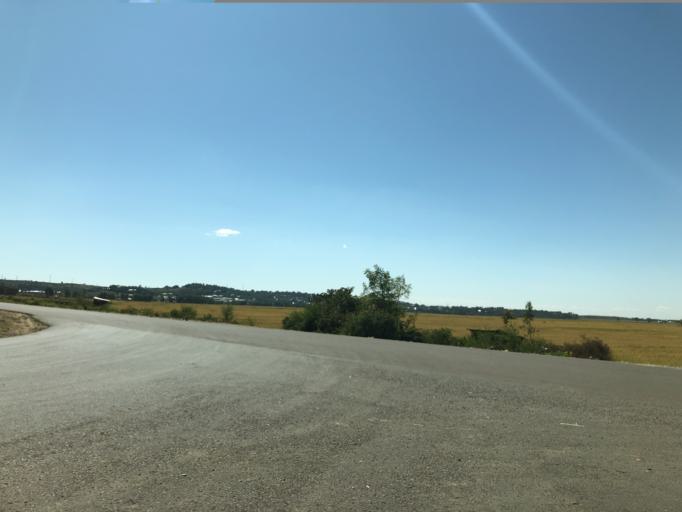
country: ET
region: Amhara
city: Werota
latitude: 11.9505
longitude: 37.7101
